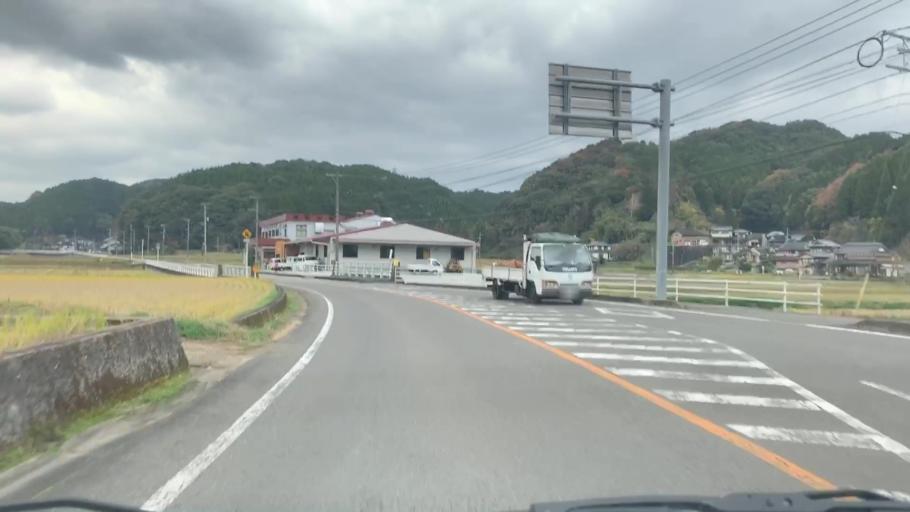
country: JP
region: Saga Prefecture
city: Ureshinomachi-shimojuku
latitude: 33.1371
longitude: 129.9765
